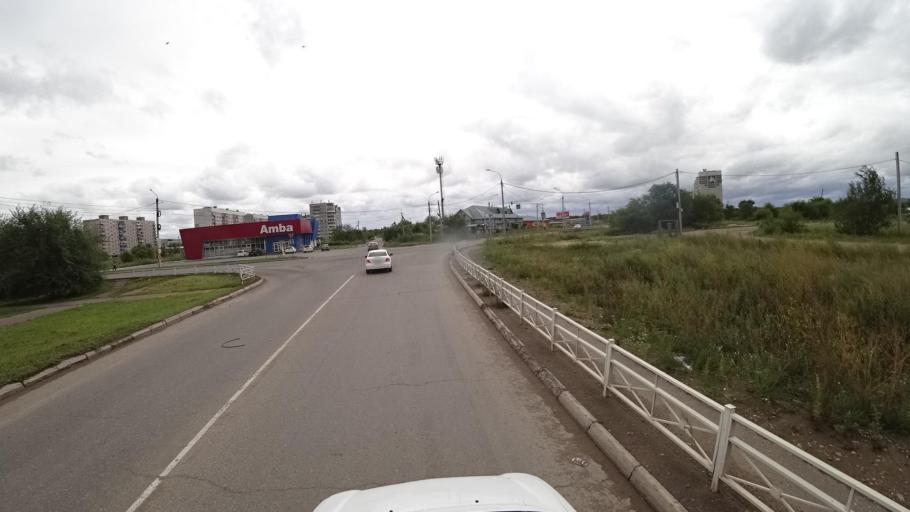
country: RU
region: Khabarovsk Krai
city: Solnechnyy
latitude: 50.5945
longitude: 137.0378
